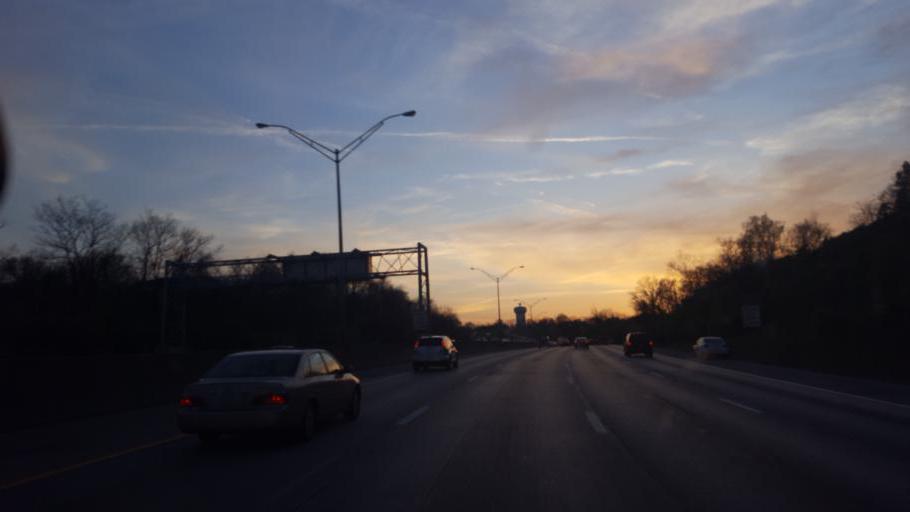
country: US
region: Kentucky
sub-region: Kenton County
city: Fort Wright
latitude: 39.0610
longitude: -84.5283
